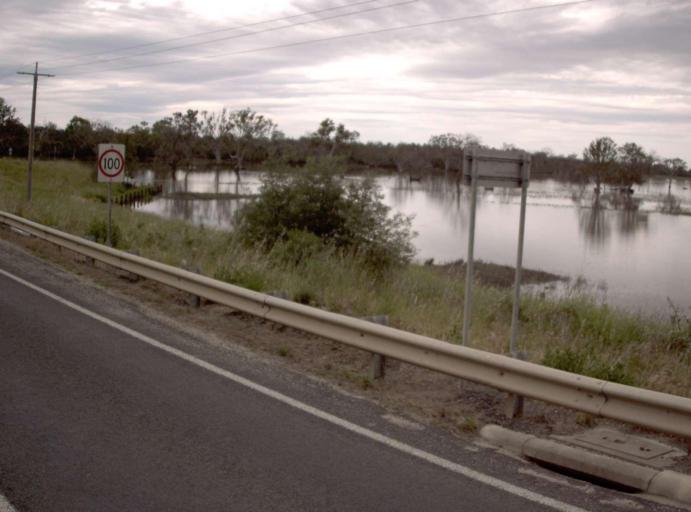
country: AU
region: Victoria
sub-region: Wellington
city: Sale
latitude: -38.1545
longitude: 147.0832
